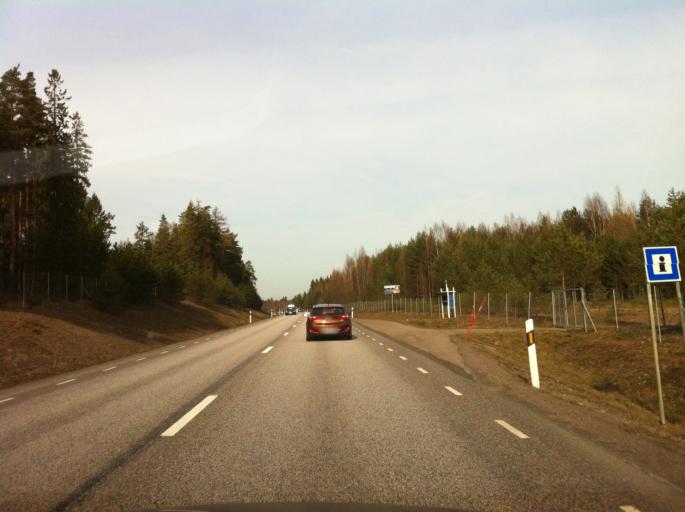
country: SE
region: Vaestra Goetaland
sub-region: Toreboda Kommun
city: Toereboda
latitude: 58.8205
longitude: 13.9855
